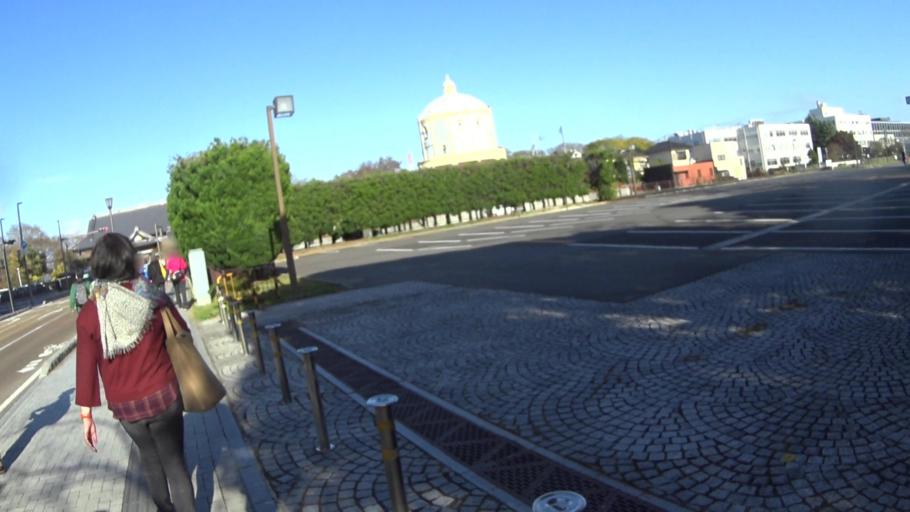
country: JP
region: Ibaraki
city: Mito-shi
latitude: 36.3774
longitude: 140.4748
